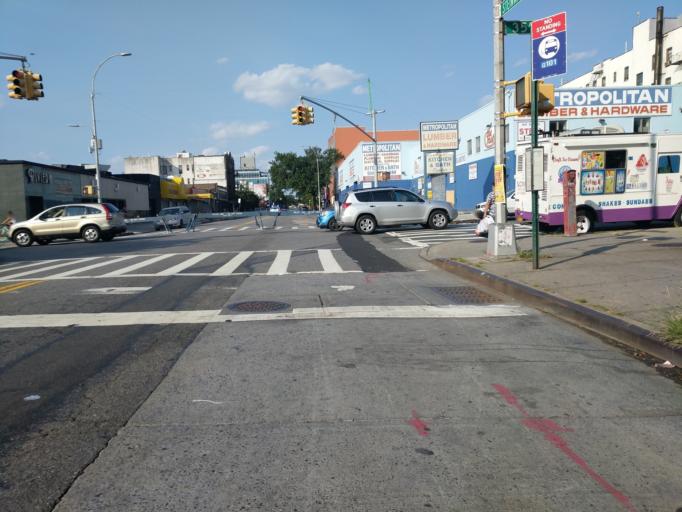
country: US
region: New York
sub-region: Queens County
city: Long Island City
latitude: 40.7550
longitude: -73.9222
